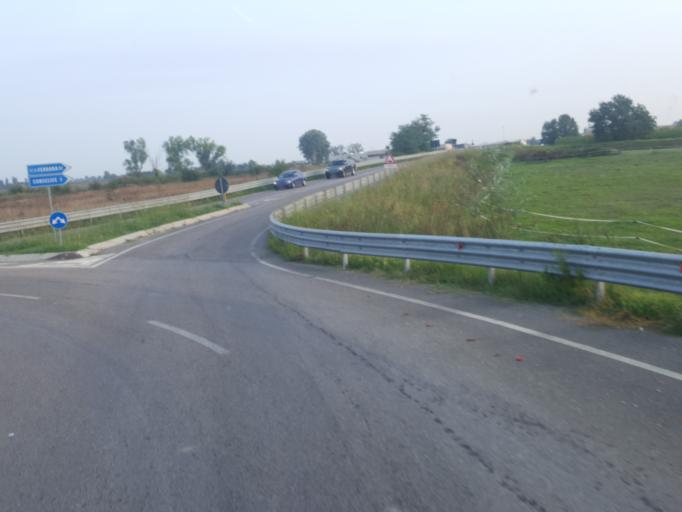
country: IT
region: Emilia-Romagna
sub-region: Provincia di Ravenna
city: Conselice
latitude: 44.4858
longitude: 11.8180
